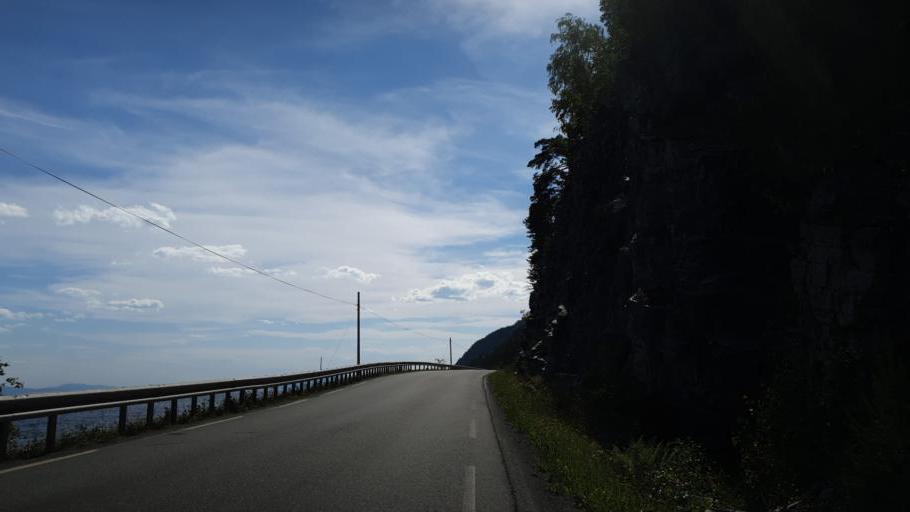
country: NO
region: Nord-Trondelag
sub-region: Leksvik
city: Leksvik
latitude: 63.6449
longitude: 10.5983
